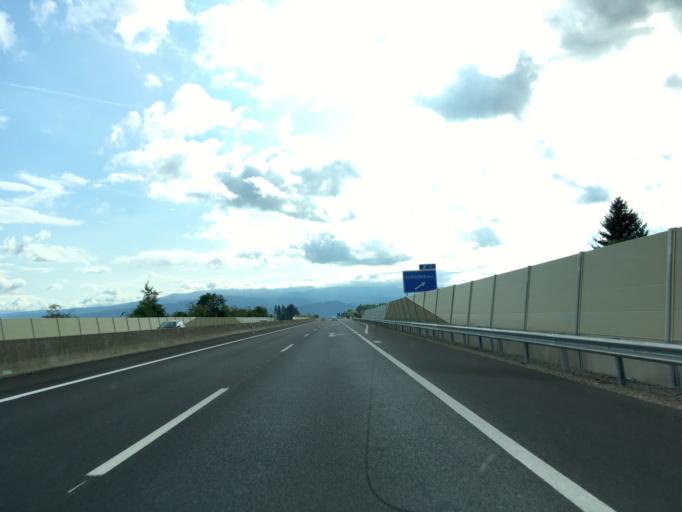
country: AT
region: Styria
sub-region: Politischer Bezirk Murtal
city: Knittelfeld
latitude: 47.2193
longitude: 14.8056
